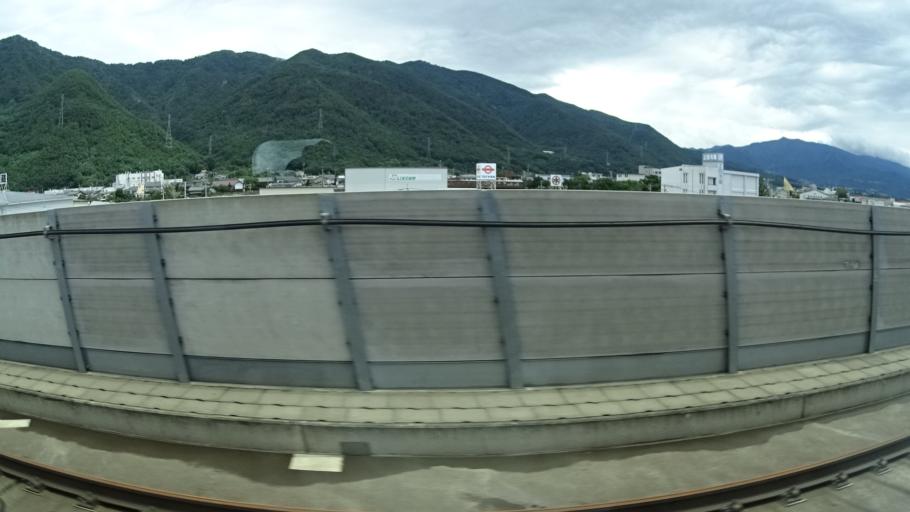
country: JP
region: Nagano
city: Ueda
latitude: 36.4171
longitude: 138.2209
